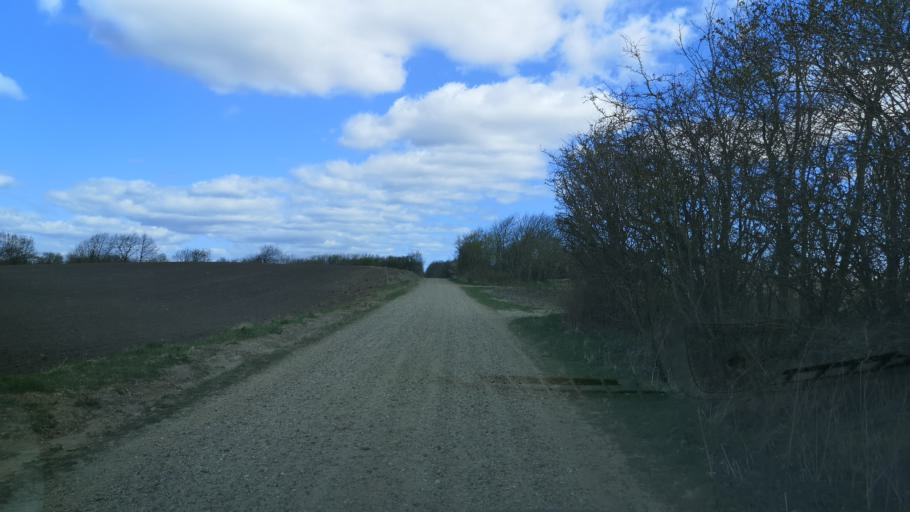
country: DK
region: Central Jutland
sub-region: Ringkobing-Skjern Kommune
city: Skjern
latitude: 55.9839
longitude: 8.5140
